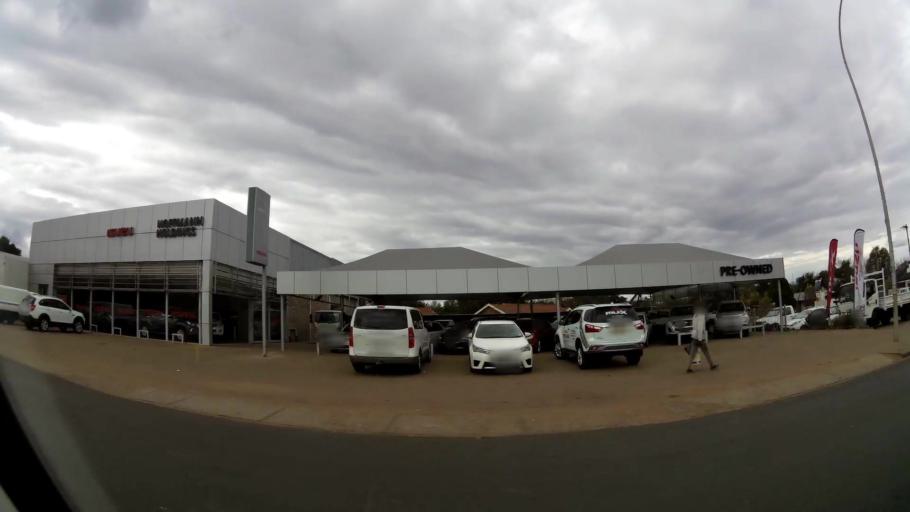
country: ZA
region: Limpopo
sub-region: Waterberg District Municipality
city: Modimolle
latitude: -24.7076
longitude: 28.4128
